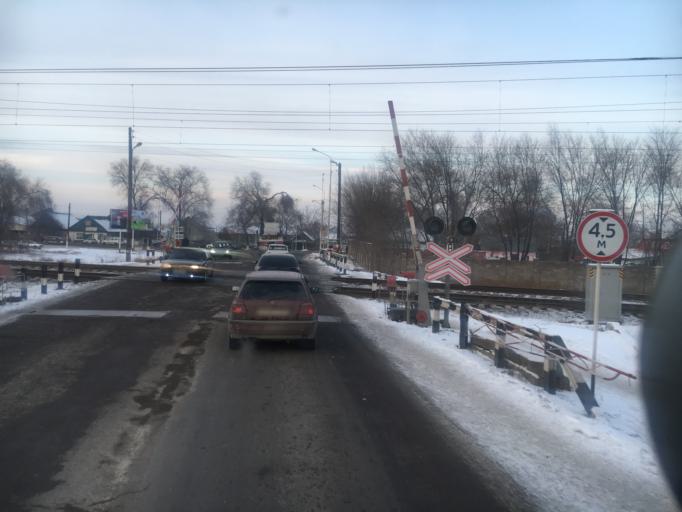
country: KZ
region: Almaty Oblysy
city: Burunday
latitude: 43.3764
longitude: 76.6419
